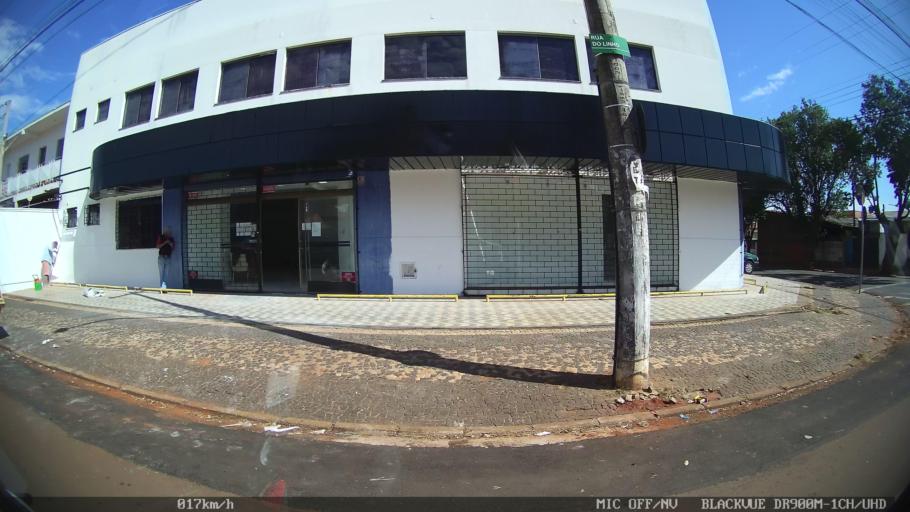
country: BR
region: Sao Paulo
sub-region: Santa Barbara D'Oeste
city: Santa Barbara d'Oeste
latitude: -22.7375
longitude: -47.3800
